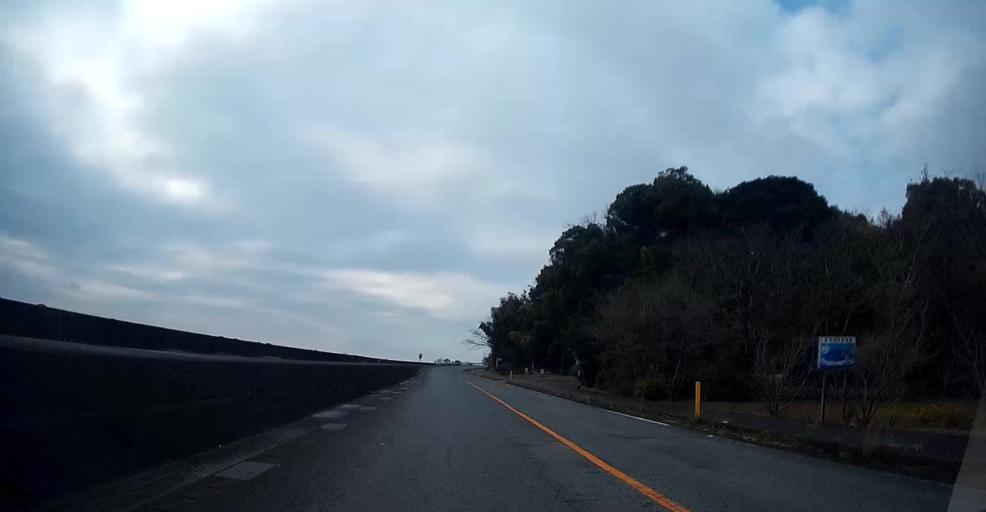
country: JP
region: Kumamoto
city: Matsubase
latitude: 32.6372
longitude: 130.6394
